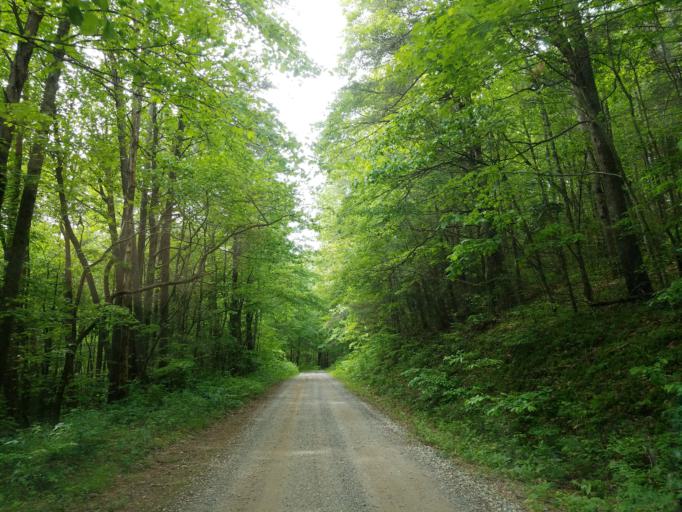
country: US
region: Georgia
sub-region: Union County
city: Blairsville
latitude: 34.7491
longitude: -83.9945
